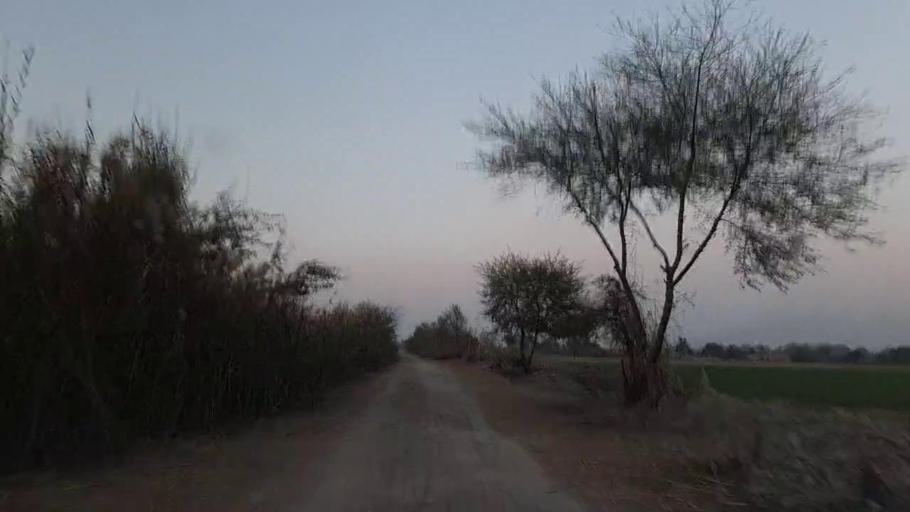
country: PK
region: Sindh
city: Bandhi
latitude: 26.6120
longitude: 68.3752
